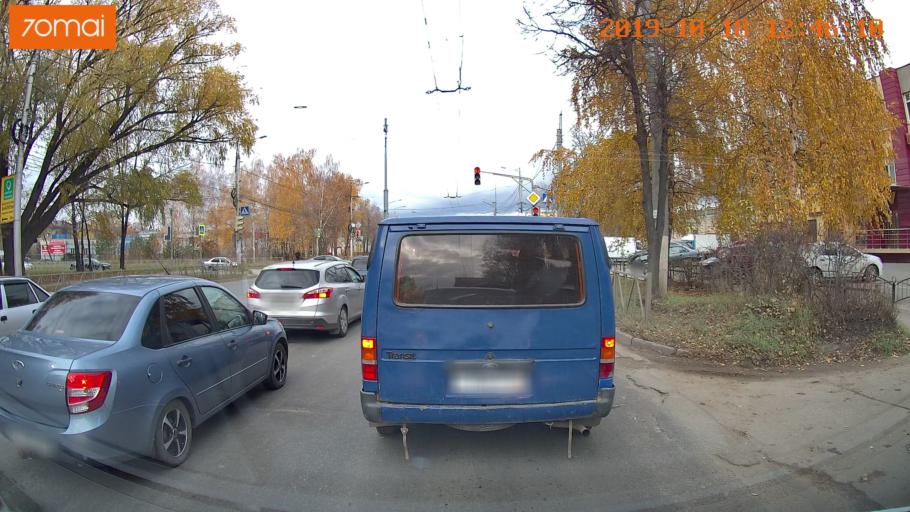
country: RU
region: Rjazan
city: Ryazan'
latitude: 54.6546
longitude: 39.6650
